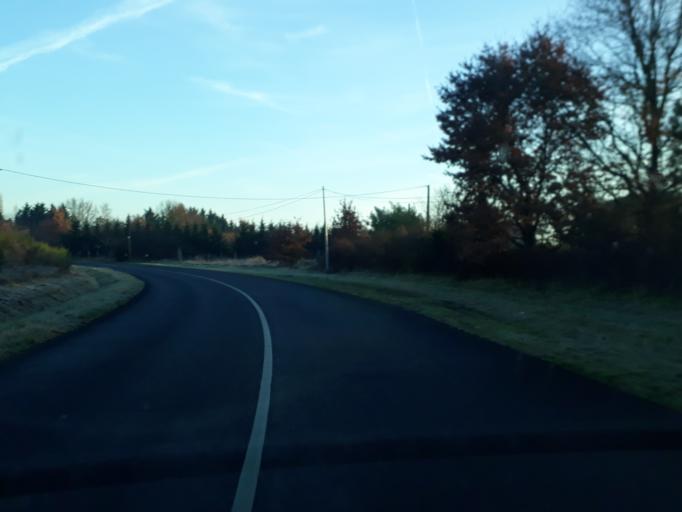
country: FR
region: Midi-Pyrenees
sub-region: Departement de la Haute-Garonne
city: Marquefave
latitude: 43.3299
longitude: 1.2324
